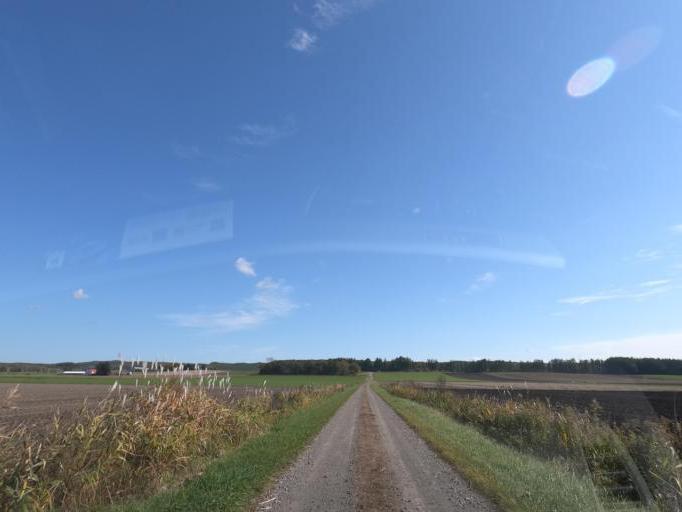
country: JP
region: Hokkaido
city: Otofuke
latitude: 43.0321
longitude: 143.2682
